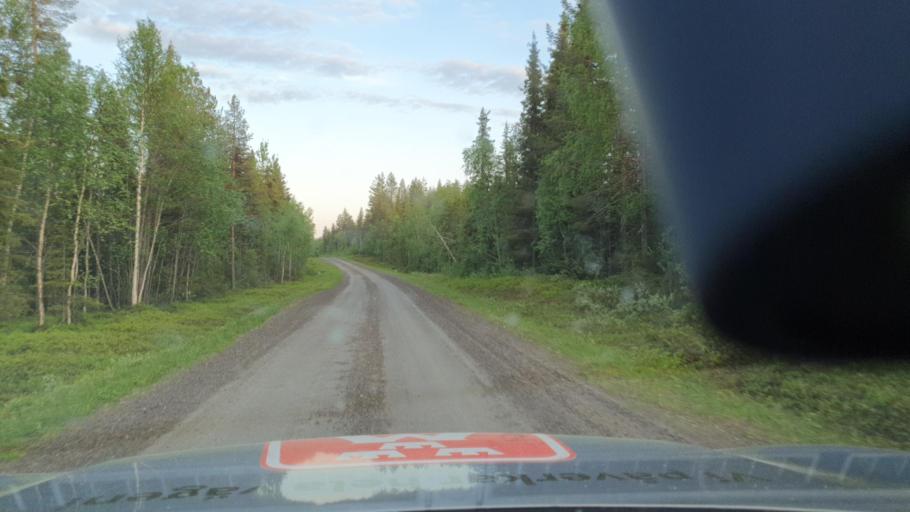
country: SE
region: Norrbotten
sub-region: Bodens Kommun
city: Boden
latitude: 66.4630
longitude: 21.6407
